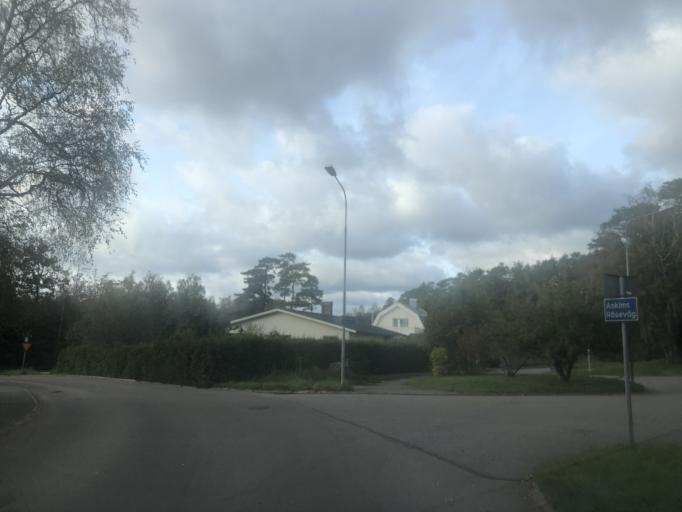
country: SE
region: Vaestra Goetaland
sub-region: Goteborg
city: Billdal
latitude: 57.6307
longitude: 11.9464
